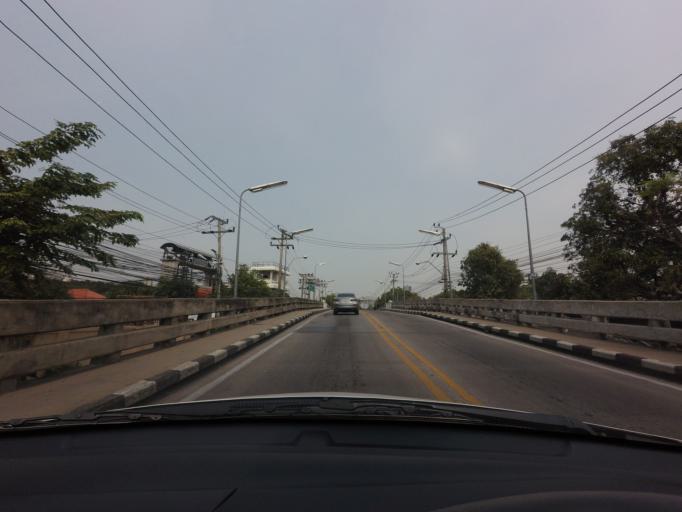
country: TH
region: Bangkok
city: Taling Chan
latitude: 13.7785
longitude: 100.4652
